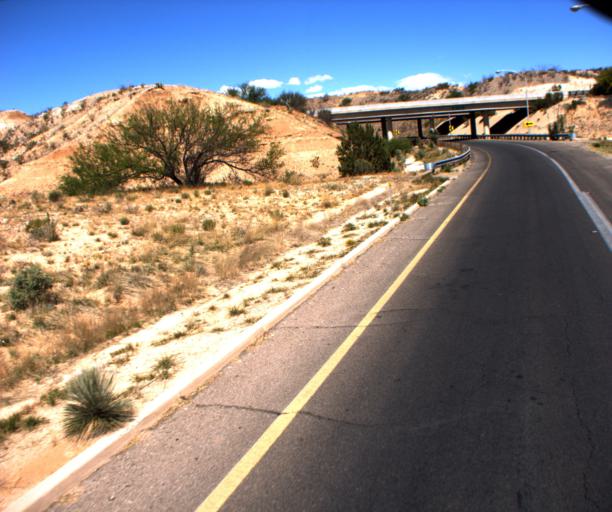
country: US
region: Arizona
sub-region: Cochise County
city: Whetstone
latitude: 31.9723
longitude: -110.3227
